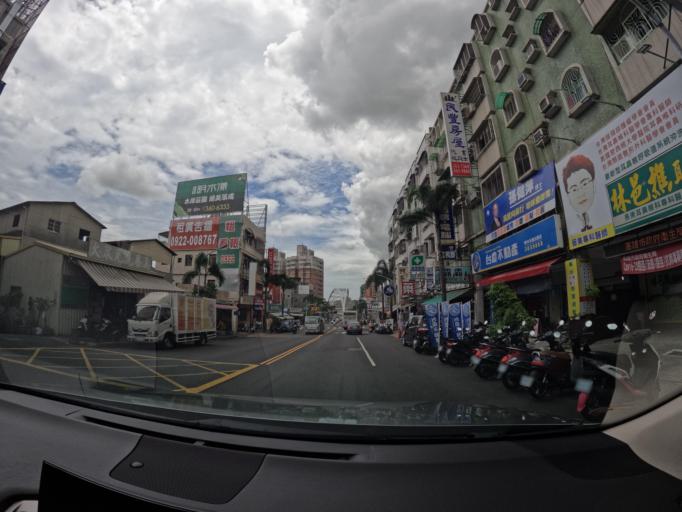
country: TW
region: Kaohsiung
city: Kaohsiung
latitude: 22.7236
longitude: 120.2976
